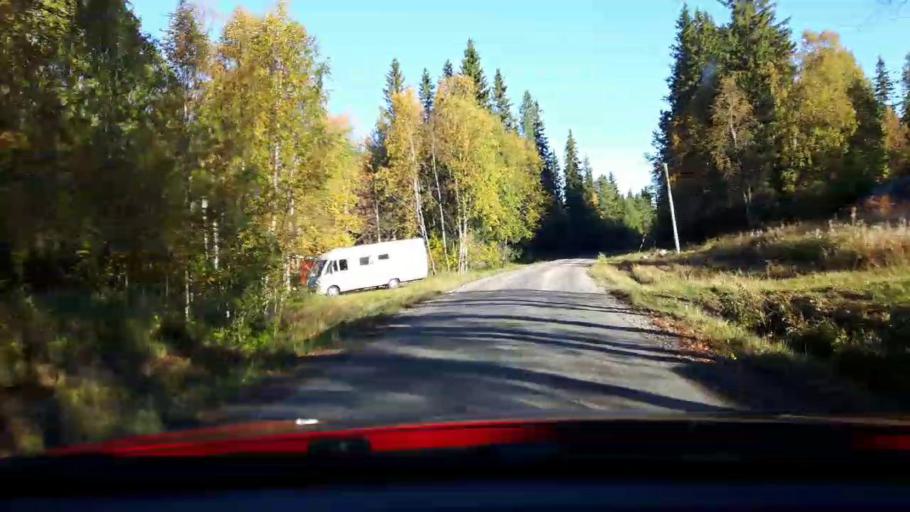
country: SE
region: Jaemtland
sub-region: Stroemsunds Kommun
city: Stroemsund
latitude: 64.3987
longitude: 15.1442
